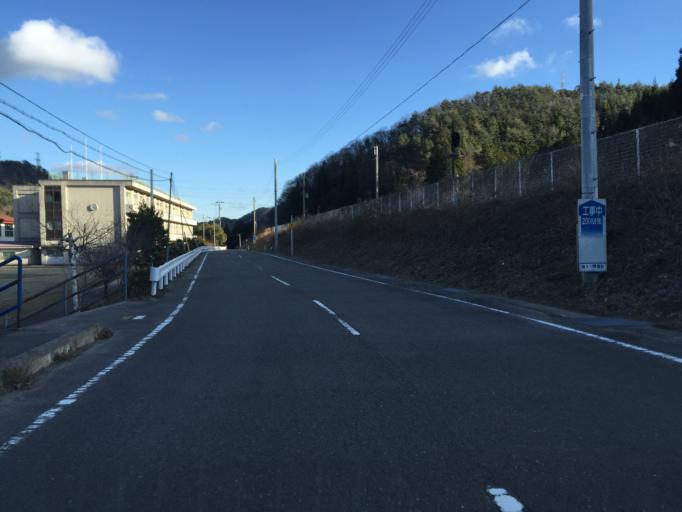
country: JP
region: Fukushima
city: Iwaki
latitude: 37.2056
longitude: 140.7515
